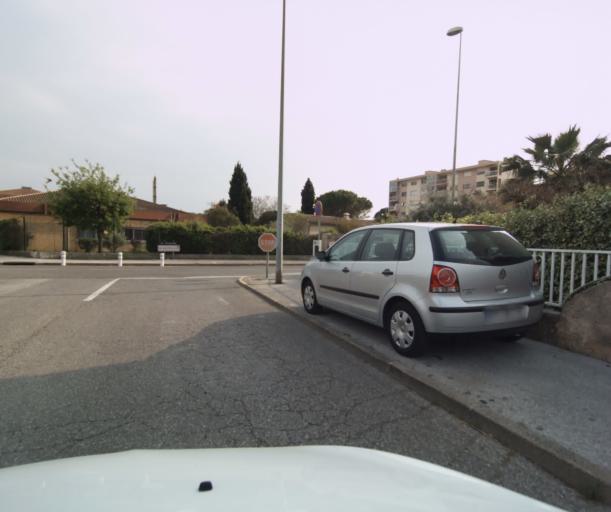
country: FR
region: Provence-Alpes-Cote d'Azur
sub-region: Departement du Var
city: La Valette-du-Var
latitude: 43.1343
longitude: 5.9938
